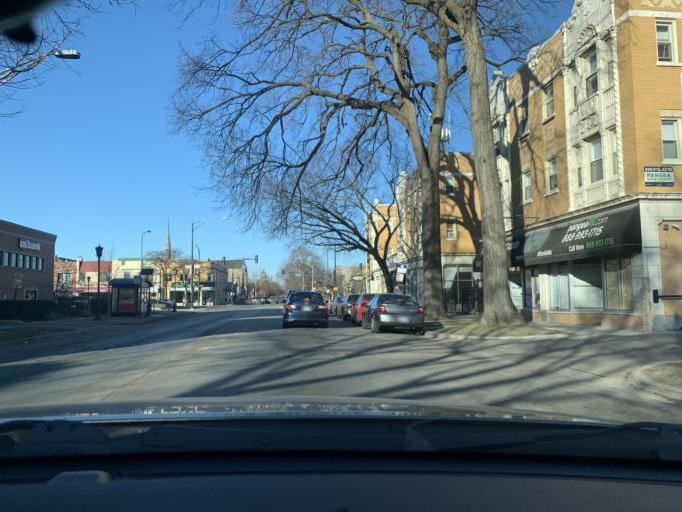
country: US
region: Illinois
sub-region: Cook County
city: Oak Park
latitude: 41.8793
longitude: -87.7747
